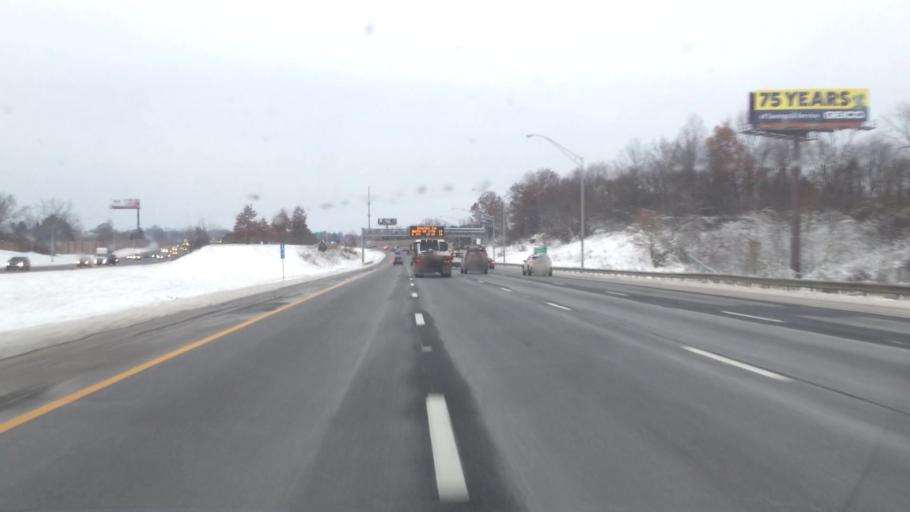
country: US
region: Ohio
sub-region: Cuyahoga County
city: Garfield Heights
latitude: 41.4218
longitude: -81.5864
